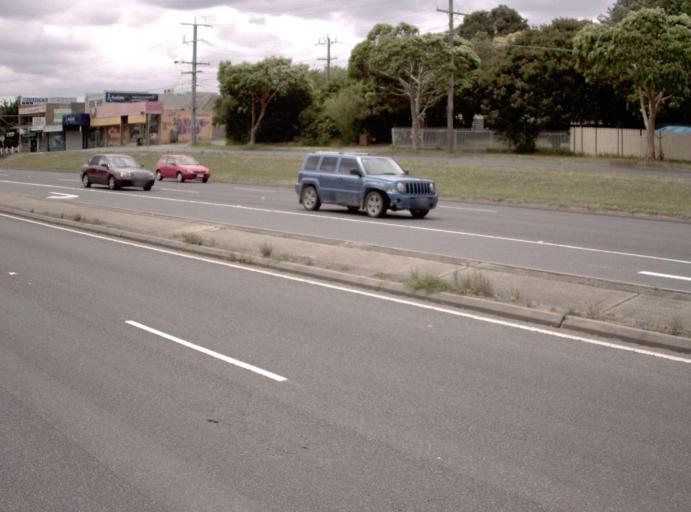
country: AU
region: Victoria
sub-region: Maroondah
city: Croydon Hills
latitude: -37.7873
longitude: 145.2736
